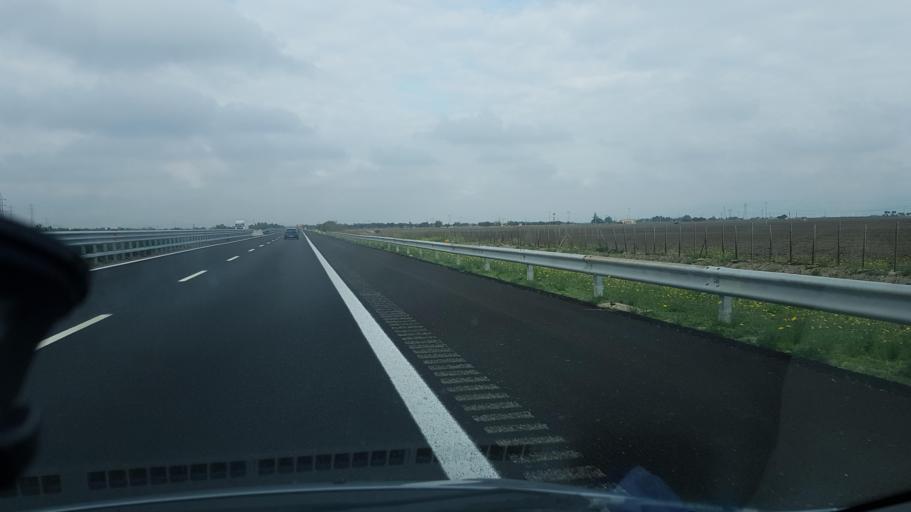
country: IT
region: Apulia
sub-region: Provincia di Foggia
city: Foggia
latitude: 41.4812
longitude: 15.5920
